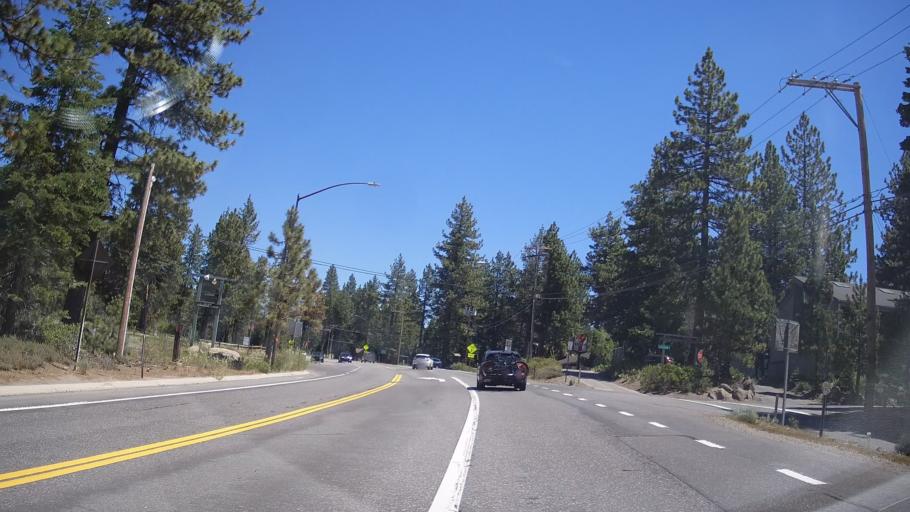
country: US
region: California
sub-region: Placer County
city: Dollar Point
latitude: 39.1907
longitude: -120.1067
